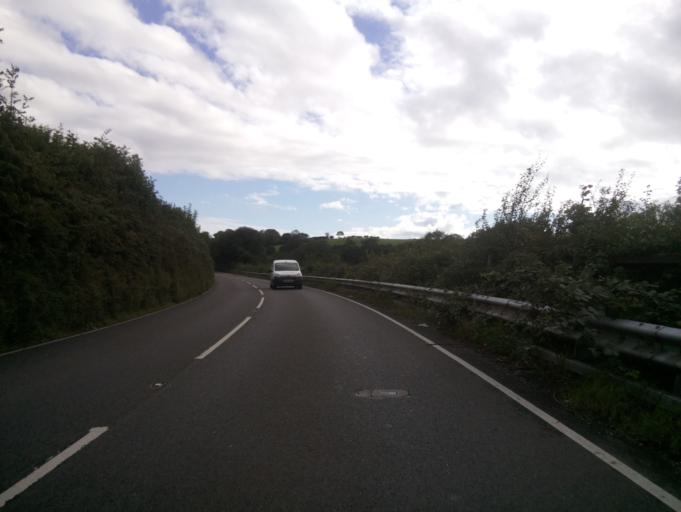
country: GB
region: England
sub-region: Devon
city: Modbury
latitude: 50.3254
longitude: -3.8430
